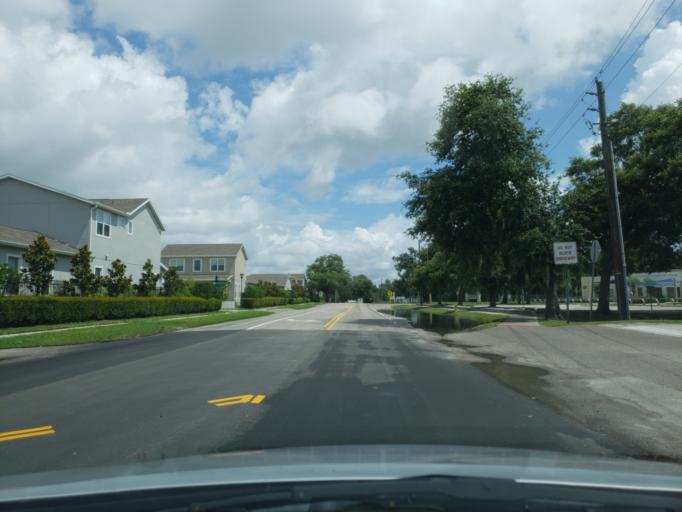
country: US
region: Florida
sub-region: Hillsborough County
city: Riverview
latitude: 27.8879
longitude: -82.3103
